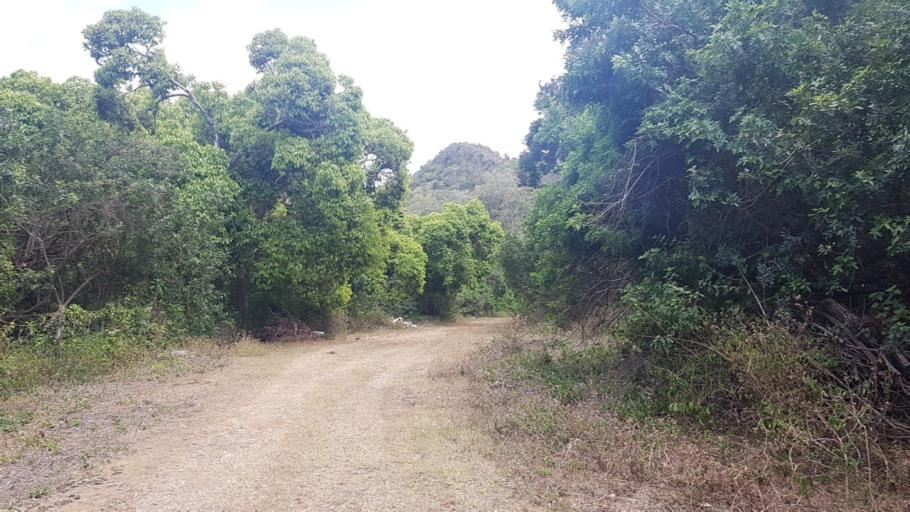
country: NC
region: South Province
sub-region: Dumbea
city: Dumbea
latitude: -22.1775
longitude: 166.4769
